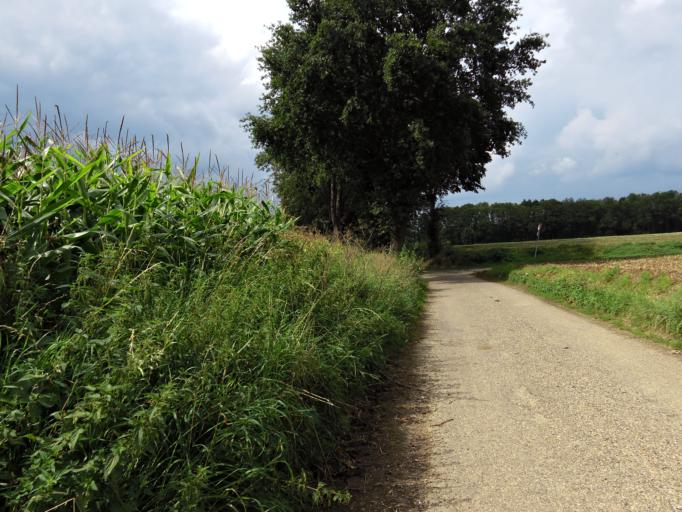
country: NL
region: Limburg
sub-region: Gemeente Simpelveld
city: Simpelveld
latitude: 50.8336
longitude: 5.9986
